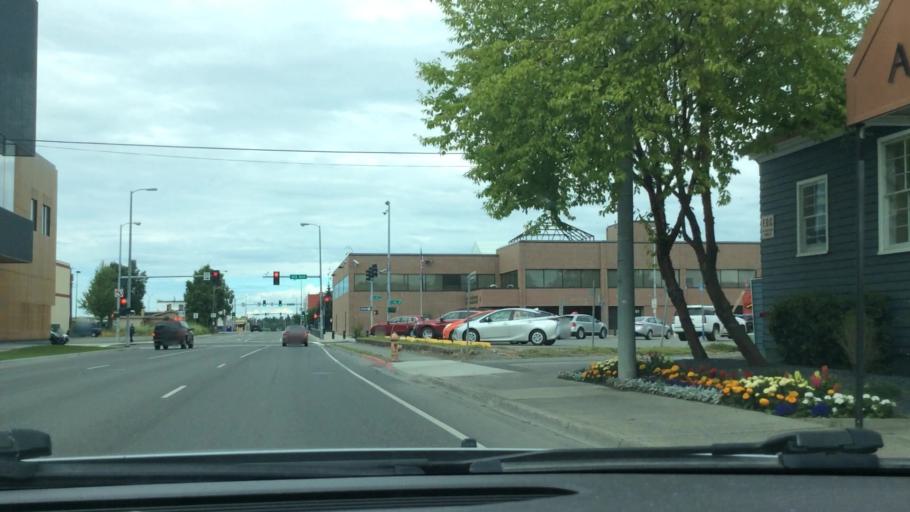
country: US
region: Alaska
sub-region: Anchorage Municipality
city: Anchorage
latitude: 61.2158
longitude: -149.8832
